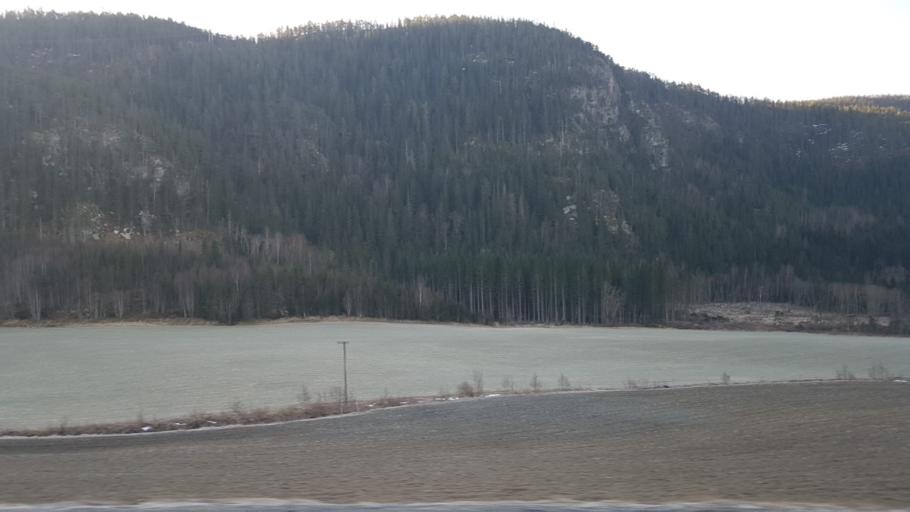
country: NO
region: Nord-Trondelag
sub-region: Stjordal
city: Stjordalshalsen
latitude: 63.5940
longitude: 11.0172
